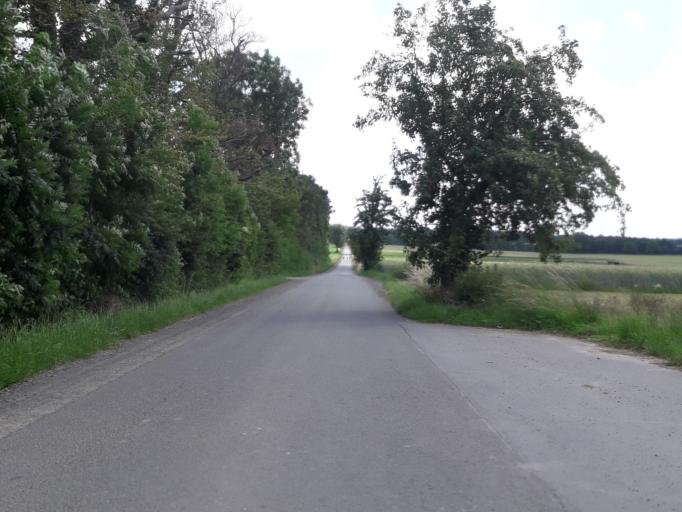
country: DE
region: North Rhine-Westphalia
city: Bad Lippspringe
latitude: 51.7390
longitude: 8.7982
